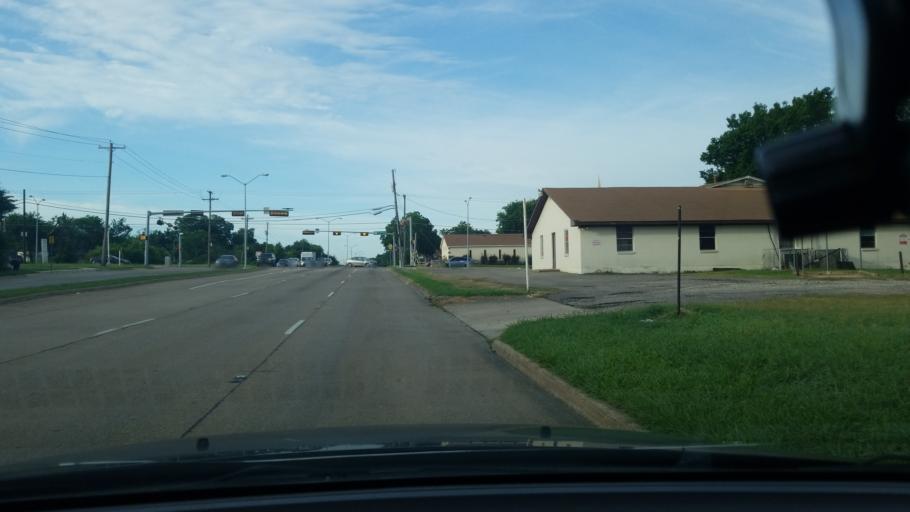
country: US
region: Texas
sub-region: Dallas County
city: Balch Springs
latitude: 32.7633
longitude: -96.6482
